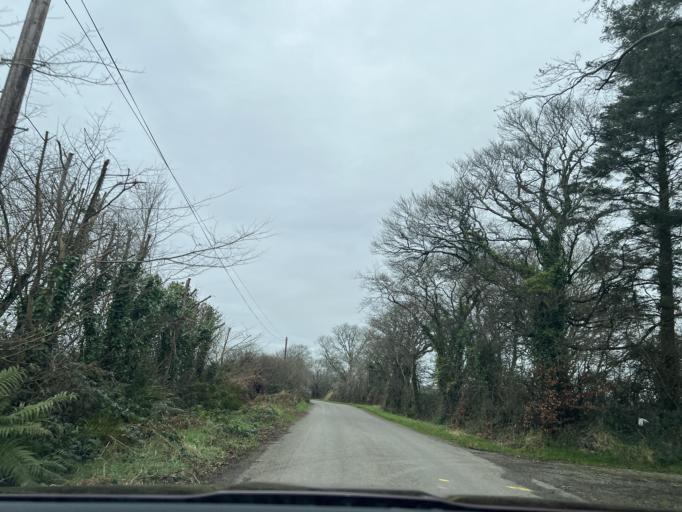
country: IE
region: Leinster
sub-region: Loch Garman
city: Loch Garman
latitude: 52.3696
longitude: -6.5219
